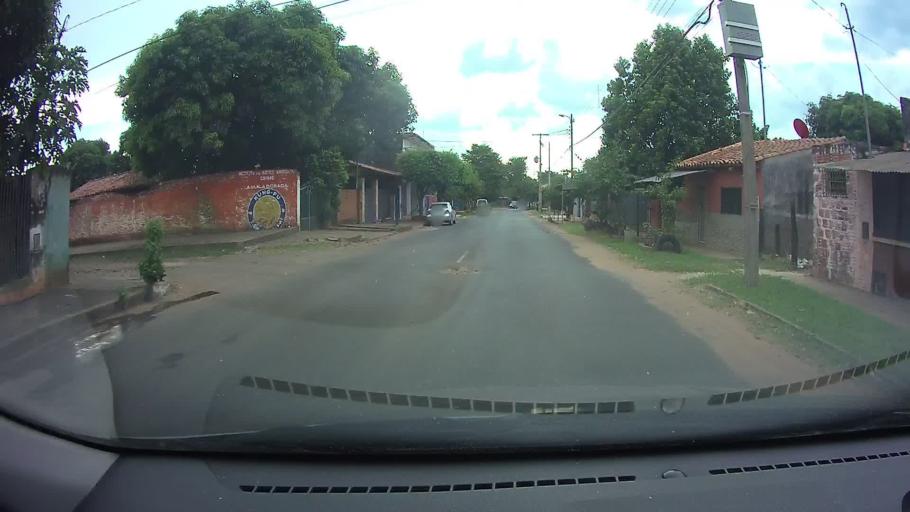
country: PY
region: Central
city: San Lorenzo
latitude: -25.2756
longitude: -57.4916
